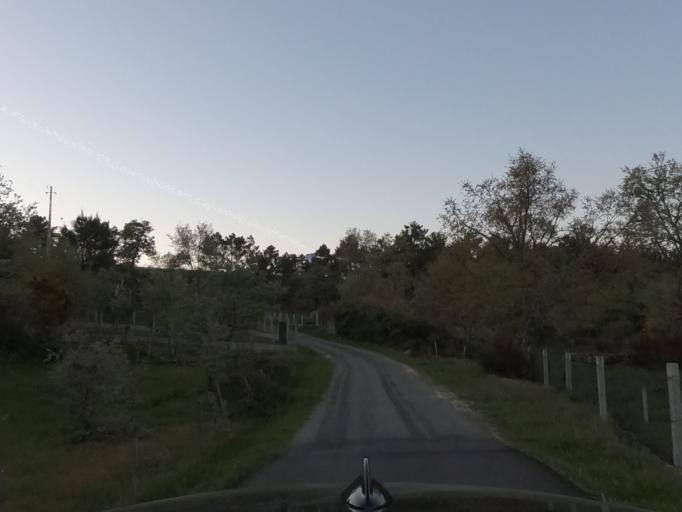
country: PT
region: Vila Real
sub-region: Vila Real
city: Vila Real
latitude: 41.3068
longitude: -7.6675
